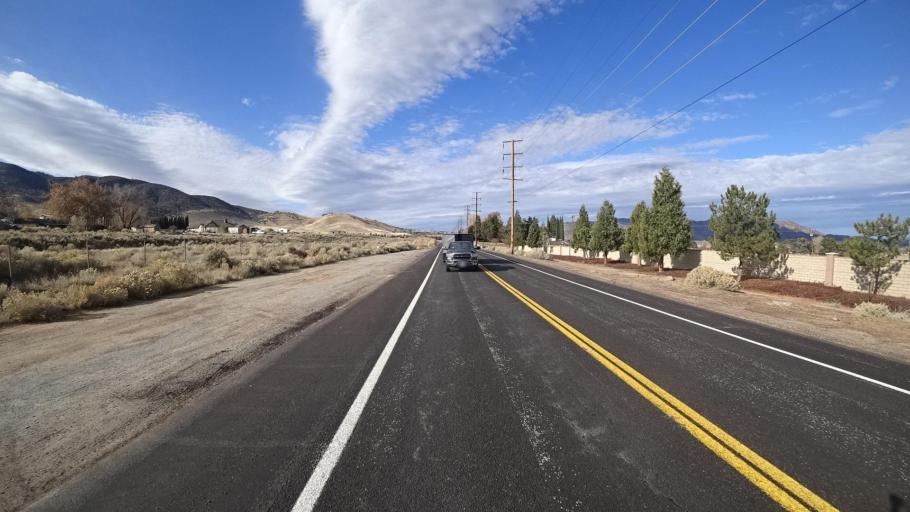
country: US
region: California
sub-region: Kern County
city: Tehachapi
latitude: 35.1095
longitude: -118.4571
